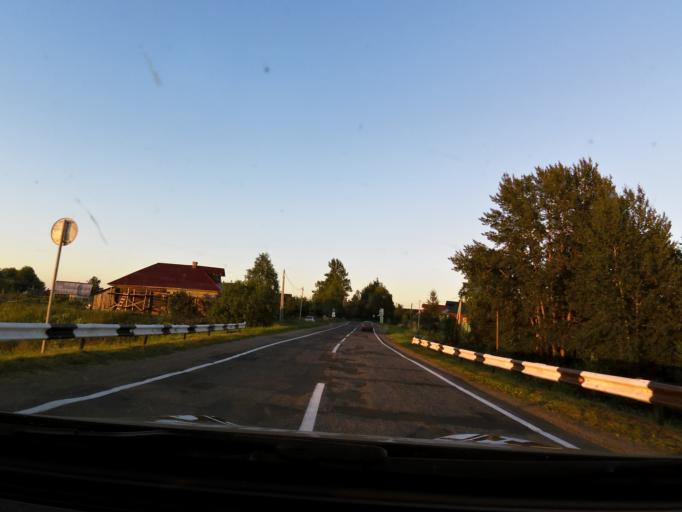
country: RU
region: Jaroslavl
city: Lyubim
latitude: 58.3559
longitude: 40.6617
